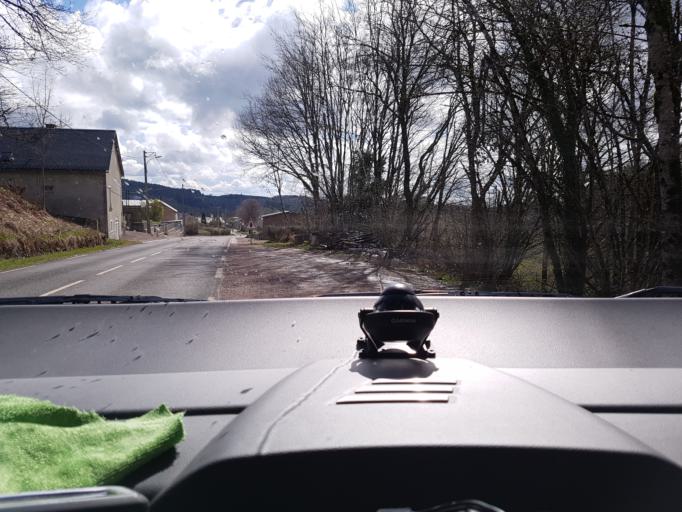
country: FR
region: Bourgogne
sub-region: Departement de la Nievre
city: Chateau-Chinon(Ville)
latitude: 47.1328
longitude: 4.0152
